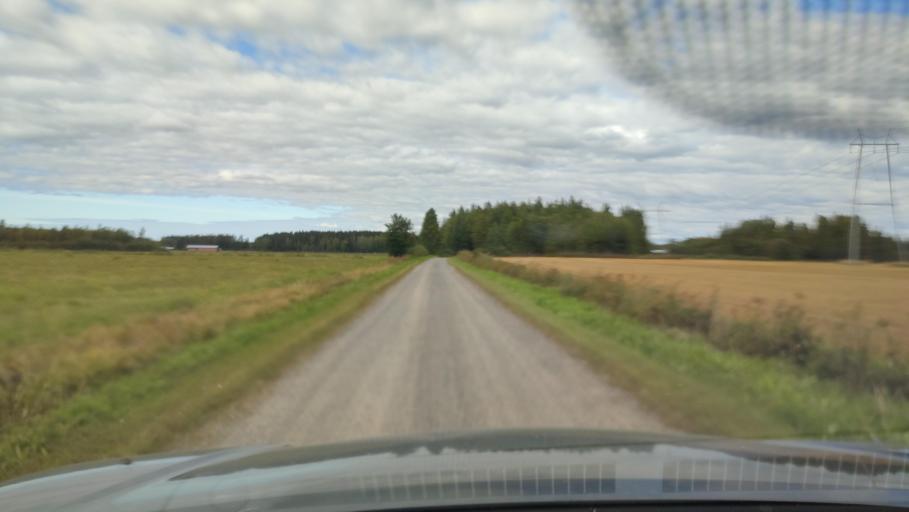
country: FI
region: Southern Ostrobothnia
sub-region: Suupohja
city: Karijoki
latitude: 62.2260
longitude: 21.6205
